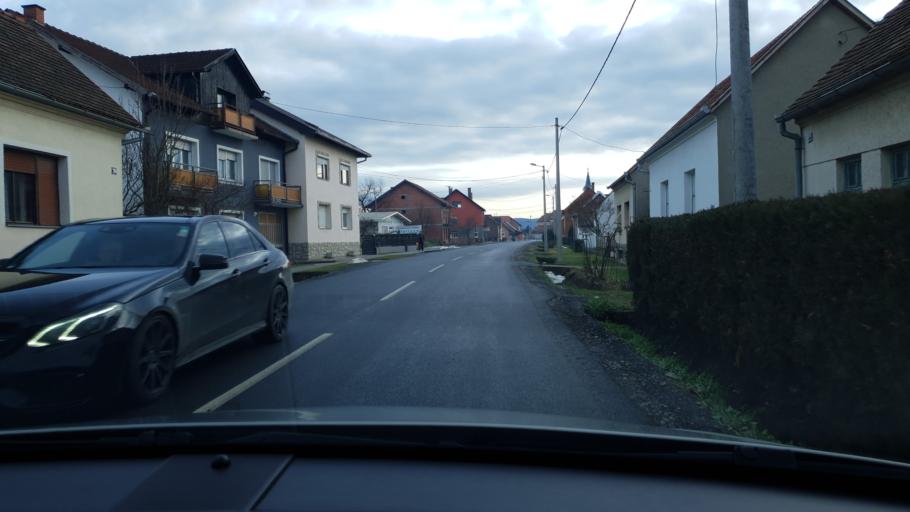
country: HR
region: Pozesko-Slavonska
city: Jaksic
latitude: 45.3605
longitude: 17.7636
